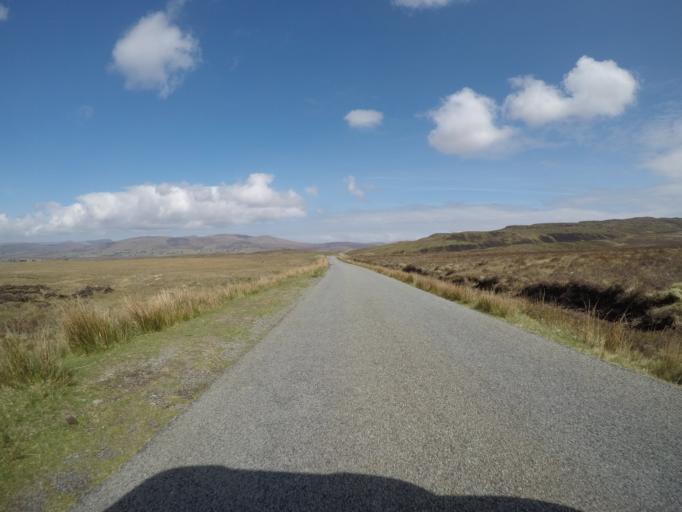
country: GB
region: Scotland
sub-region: Highland
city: Isle of Skye
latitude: 57.4199
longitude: -6.2874
